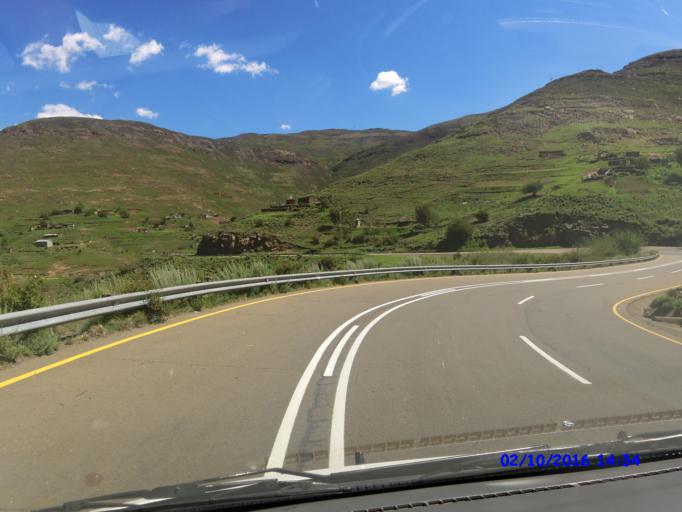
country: LS
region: Maseru
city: Nako
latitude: -29.4901
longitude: 28.0581
